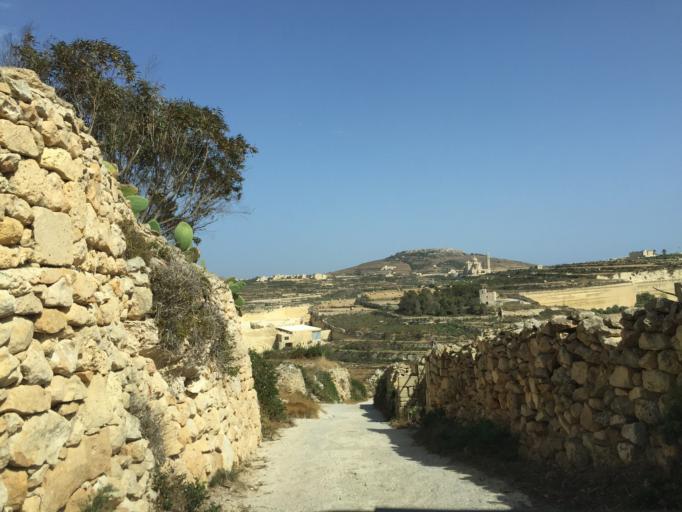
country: MT
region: L-Gharb
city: Gharb
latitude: 36.0703
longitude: 14.2059
